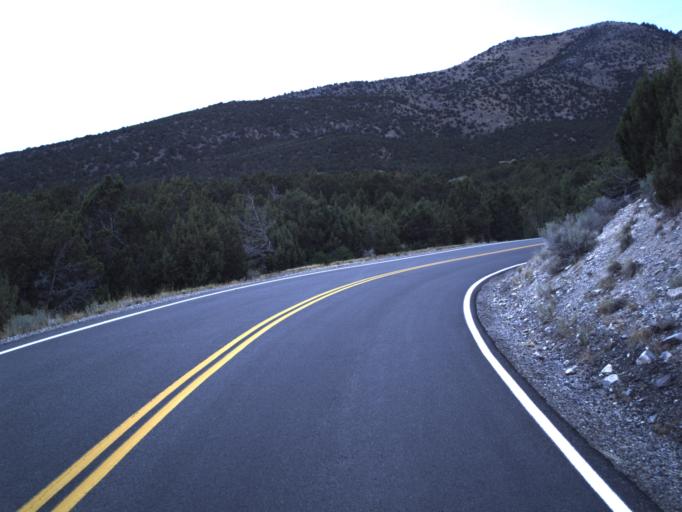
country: US
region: Utah
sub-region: Tooele County
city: Grantsville
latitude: 40.3485
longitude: -112.5562
